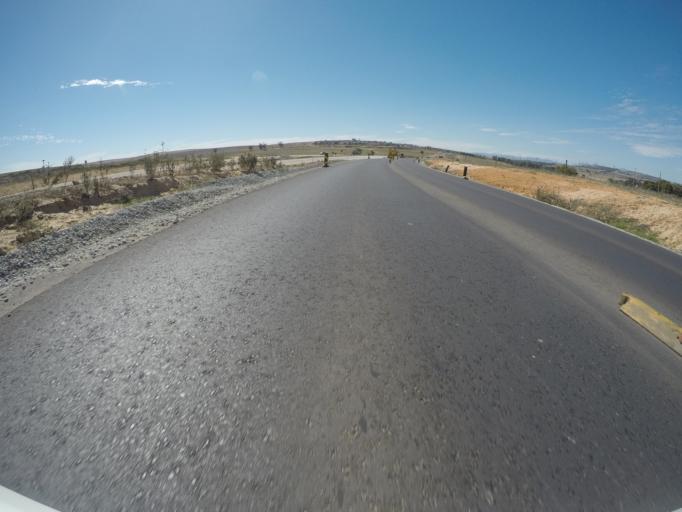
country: ZA
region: Western Cape
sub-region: West Coast District Municipality
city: Malmesbury
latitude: -33.4800
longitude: 18.6814
